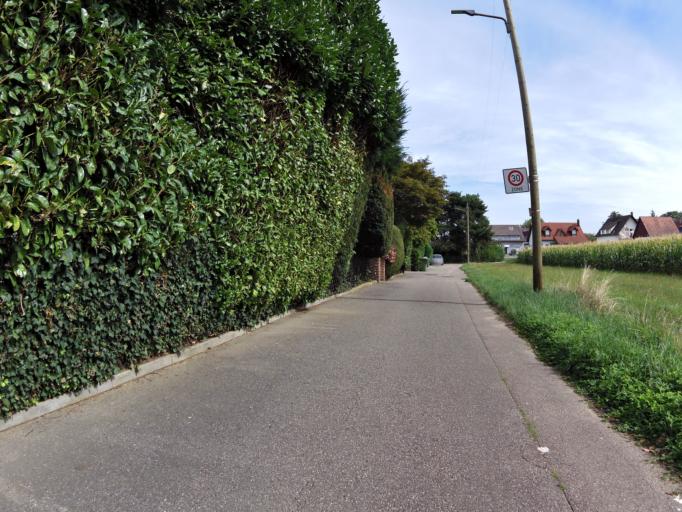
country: DE
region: Baden-Wuerttemberg
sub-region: Freiburg Region
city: Lahr
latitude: 48.3589
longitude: 7.8376
